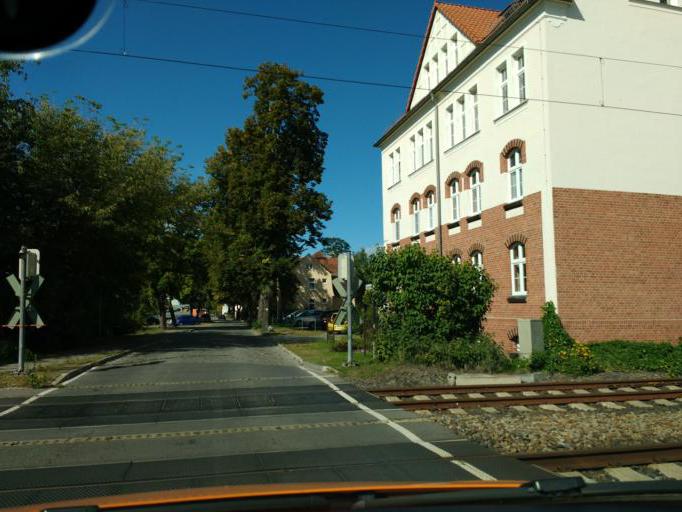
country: DE
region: Brandenburg
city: Bestensee
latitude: 52.2339
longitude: 13.6335
